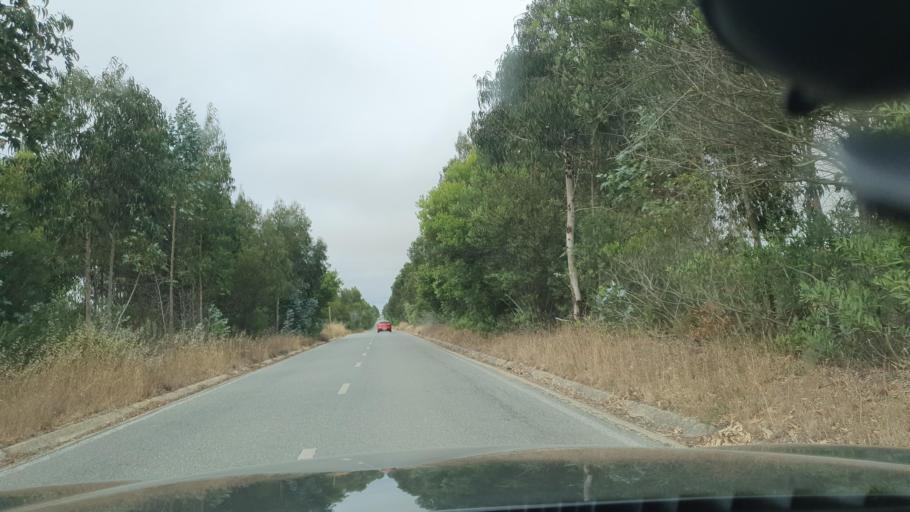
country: PT
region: Beja
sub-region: Odemira
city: Sao Teotonio
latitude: 37.5367
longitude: -8.7532
